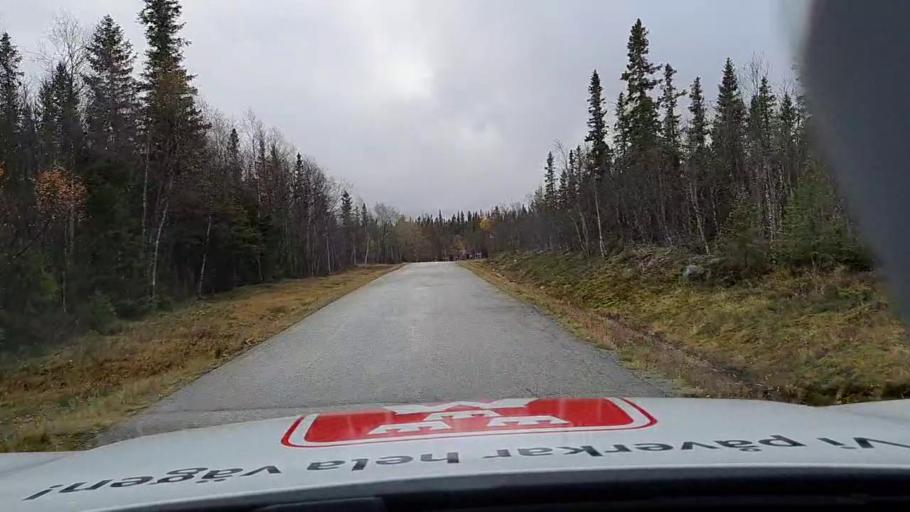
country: SE
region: Jaemtland
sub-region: Bergs Kommun
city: Hoverberg
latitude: 63.0062
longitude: 13.9453
